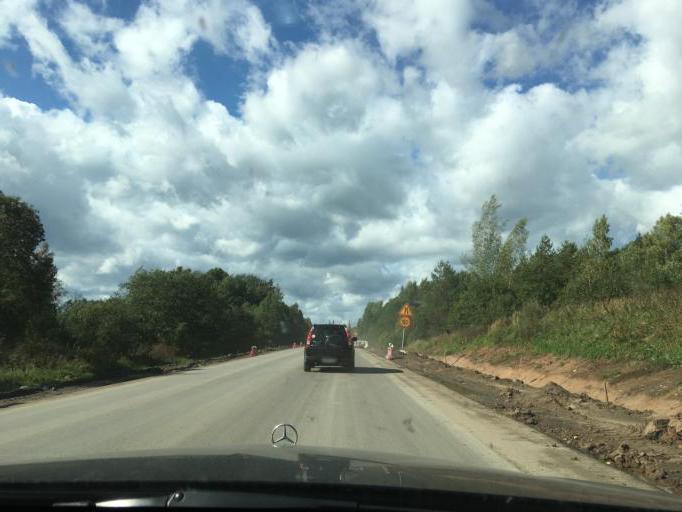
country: RU
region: Pskov
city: Novosokol'niki
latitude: 56.2810
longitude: 30.3013
